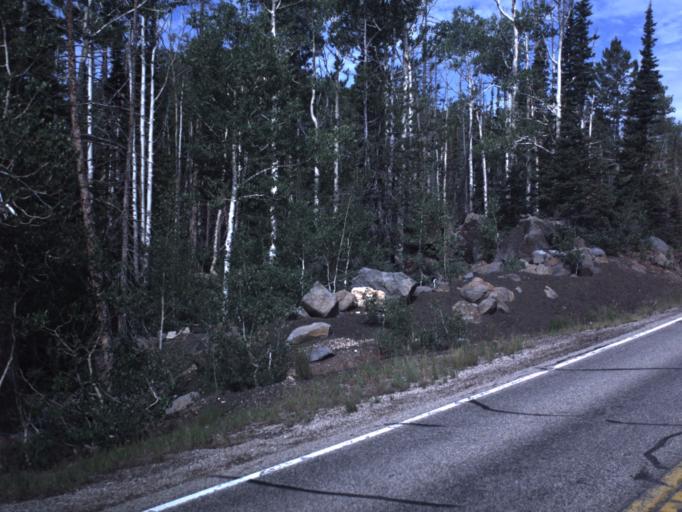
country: US
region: Utah
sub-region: Iron County
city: Parowan
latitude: 37.5390
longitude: -112.7753
